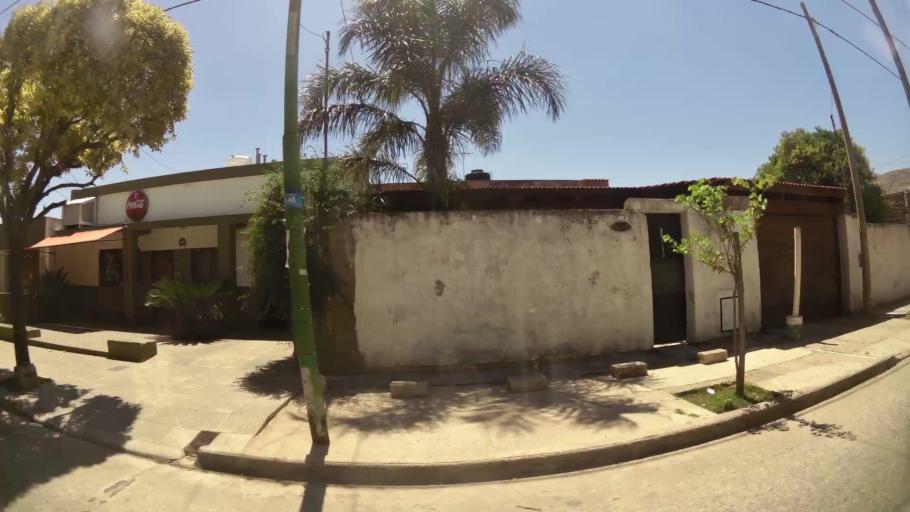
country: AR
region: Cordoba
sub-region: Departamento de Capital
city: Cordoba
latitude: -31.3914
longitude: -64.1488
